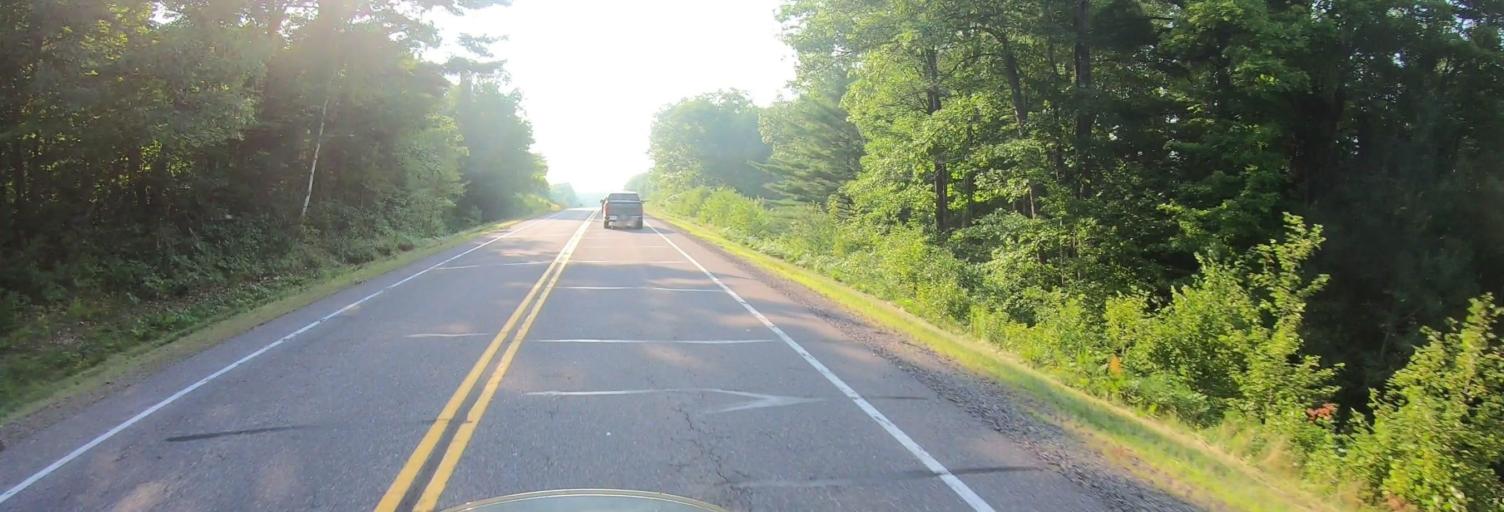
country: US
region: Wisconsin
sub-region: Sawyer County
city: Little Round Lake
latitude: 46.0651
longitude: -91.1627
